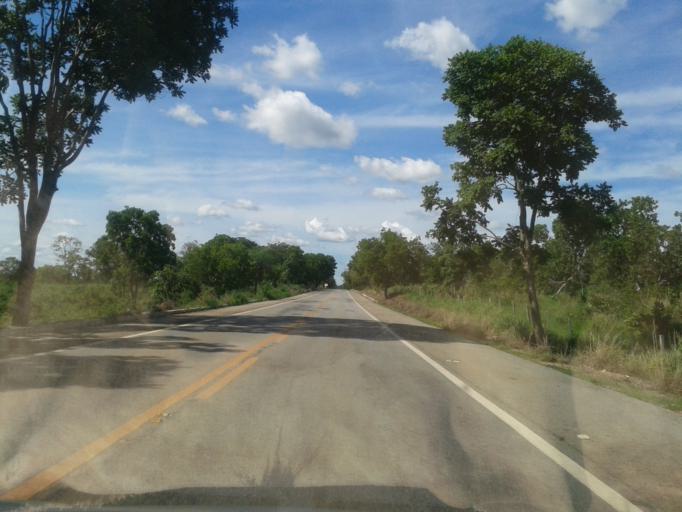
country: BR
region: Goias
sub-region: Itapuranga
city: Itapuranga
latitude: -15.4196
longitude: -50.3768
